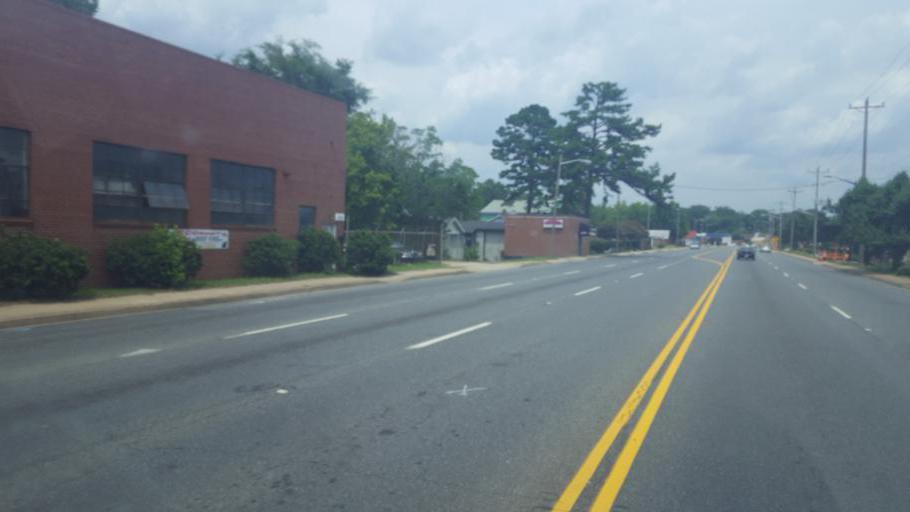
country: US
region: South Carolina
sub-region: York County
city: Rock Hill
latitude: 34.9392
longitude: -81.0395
